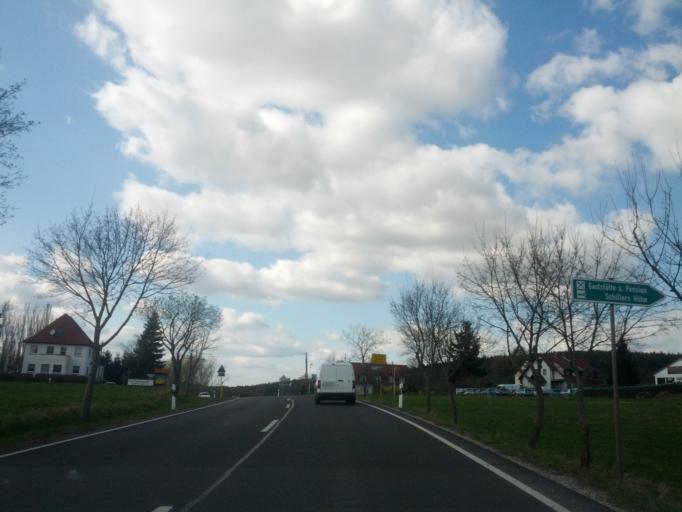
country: DE
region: Thuringia
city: Georgenthal
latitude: 50.8340
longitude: 10.6365
